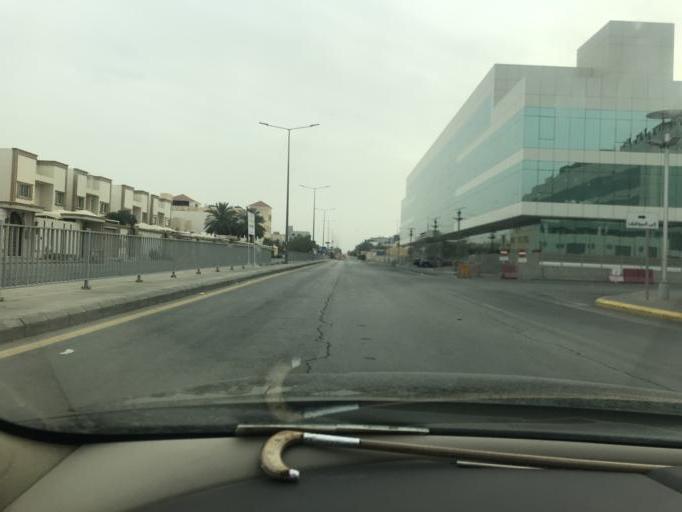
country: SA
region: Ar Riyad
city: Riyadh
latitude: 24.7201
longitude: 46.7753
